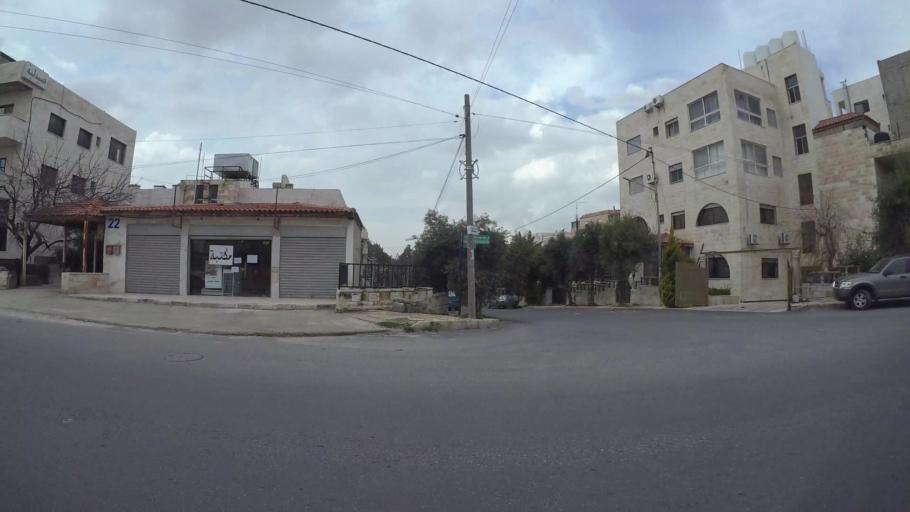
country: JO
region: Amman
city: Umm as Summaq
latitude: 31.8950
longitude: 35.8637
